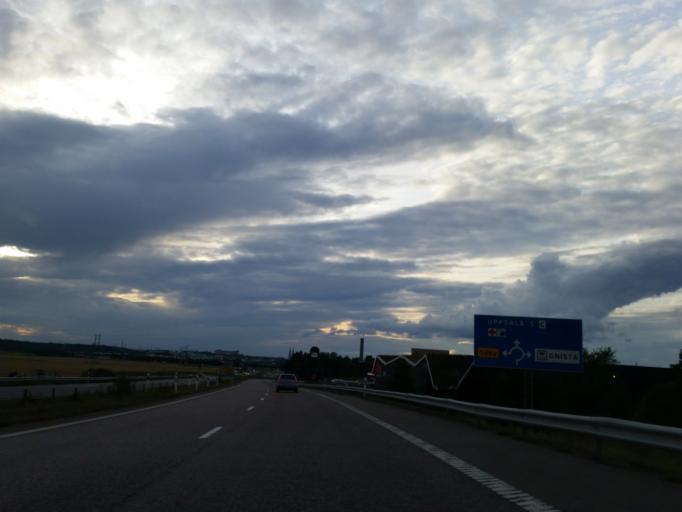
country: SE
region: Uppsala
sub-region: Uppsala Kommun
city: Saevja
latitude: 59.8420
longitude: 17.7165
